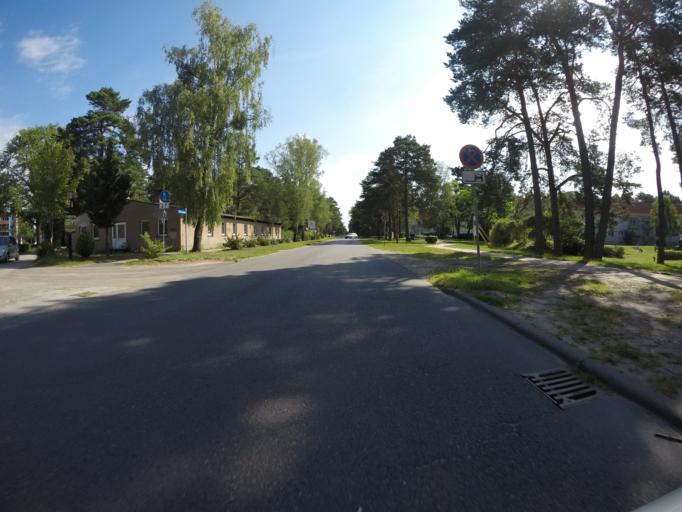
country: DE
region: Brandenburg
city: Rheinsberg
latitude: 53.0988
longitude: 12.9037
